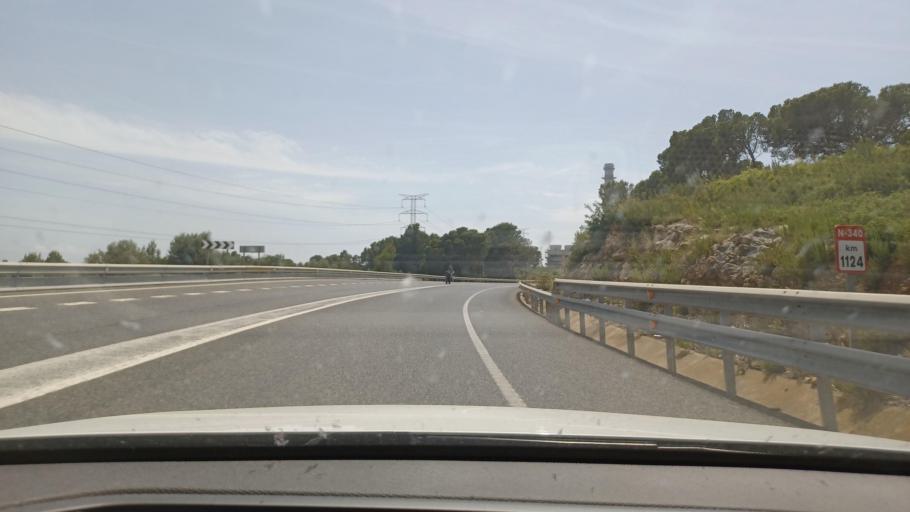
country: ES
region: Catalonia
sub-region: Provincia de Tarragona
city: l'Ametlla de Mar
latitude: 40.9623
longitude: 0.8742
